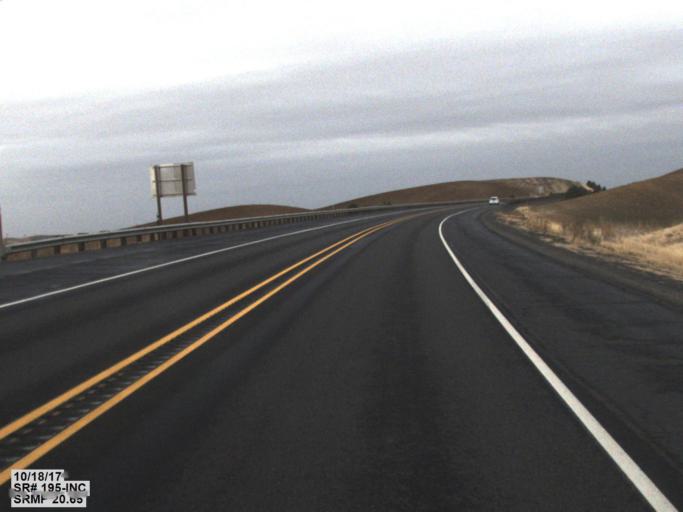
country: US
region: Washington
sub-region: Whitman County
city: Pullman
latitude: 46.7121
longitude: -117.2168
